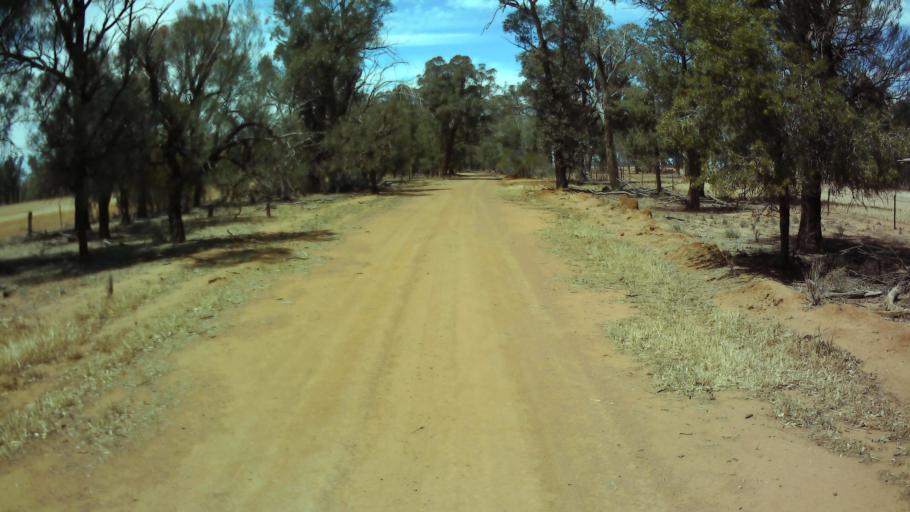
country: AU
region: New South Wales
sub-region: Weddin
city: Grenfell
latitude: -33.9094
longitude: 147.8068
